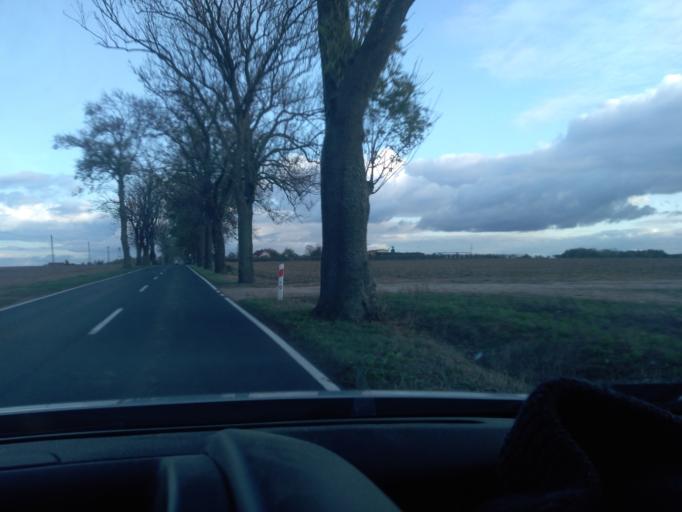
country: PL
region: Greater Poland Voivodeship
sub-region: Powiat poznanski
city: Murowana Goslina
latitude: 52.6312
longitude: 16.9700
